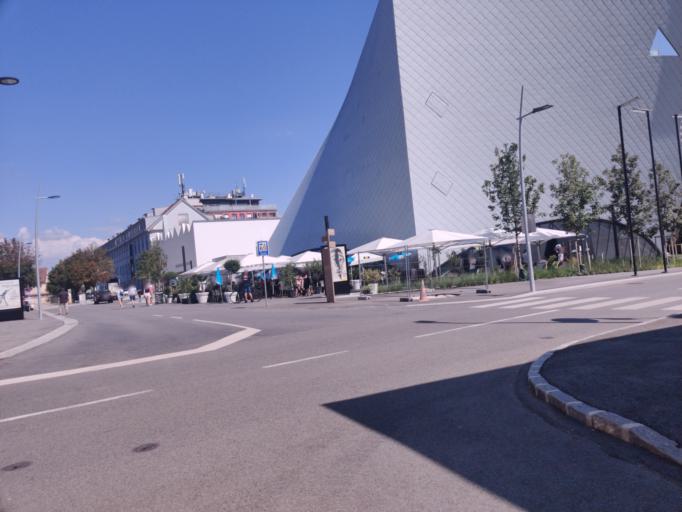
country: AT
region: Lower Austria
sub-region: Politischer Bezirk Krems
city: Weinzierl bei Krems
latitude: 48.4046
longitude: 15.5869
